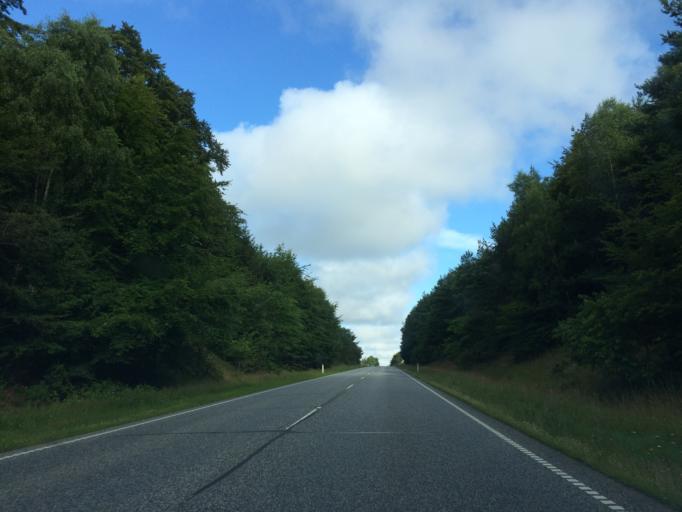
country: DK
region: Central Jutland
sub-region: Viborg Kommune
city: Bjerringbro
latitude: 56.3225
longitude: 9.5654
